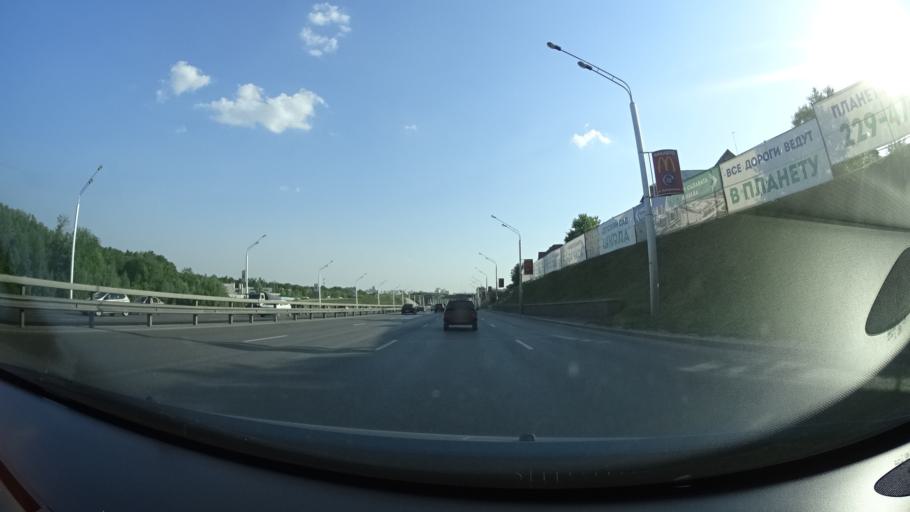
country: RU
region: Bashkortostan
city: Ufa
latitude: 54.7416
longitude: 56.0092
